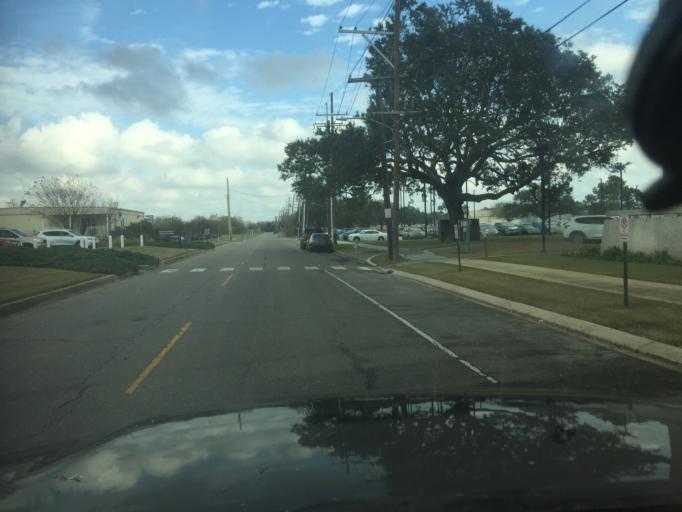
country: US
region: Louisiana
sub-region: Orleans Parish
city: New Orleans
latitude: 29.9918
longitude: -90.0838
